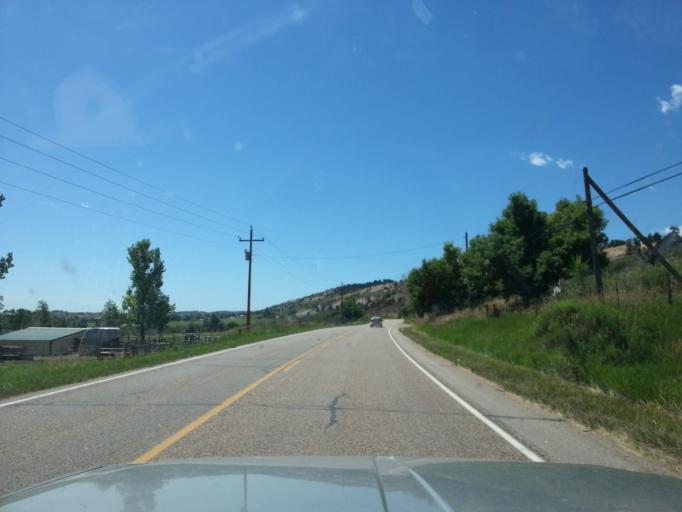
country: US
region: Colorado
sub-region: Larimer County
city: Loveland
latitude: 40.4550
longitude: -105.2050
